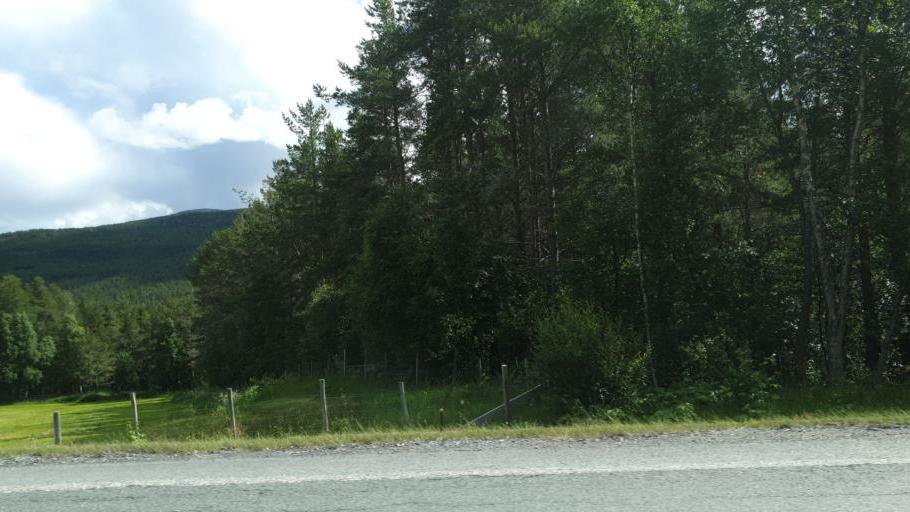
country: NO
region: Sor-Trondelag
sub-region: Rennebu
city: Berkak
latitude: 62.6746
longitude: 9.9138
